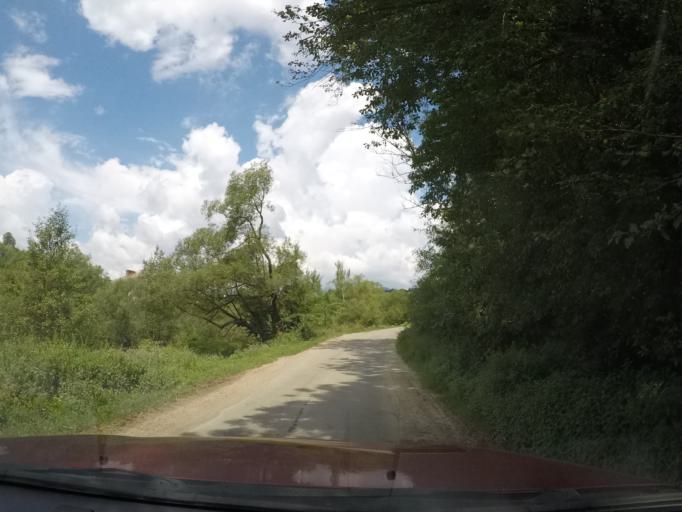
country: UA
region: Zakarpattia
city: Velykyi Bereznyi
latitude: 49.0145
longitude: 22.6212
